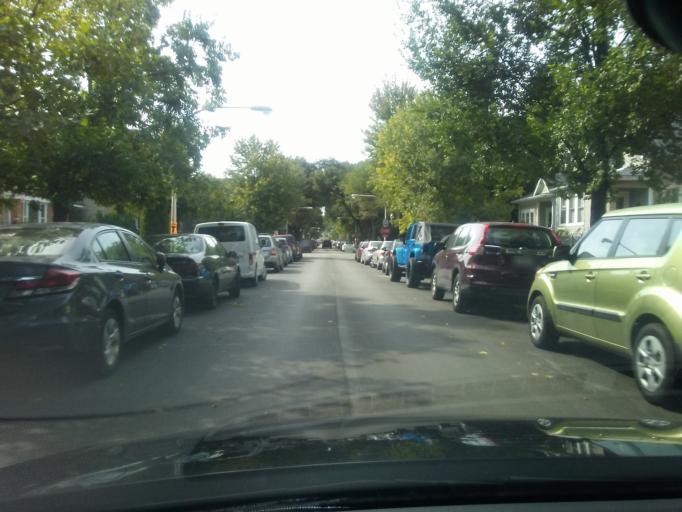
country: US
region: Illinois
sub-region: Cook County
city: Lincolnwood
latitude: 41.9385
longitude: -87.6995
